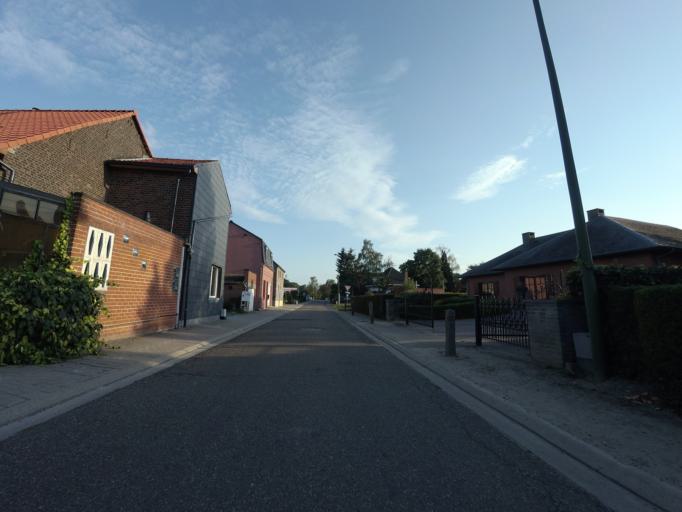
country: BE
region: Flanders
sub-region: Provincie Vlaams-Brabant
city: Boortmeerbeek
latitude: 50.9512
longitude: 4.5821
